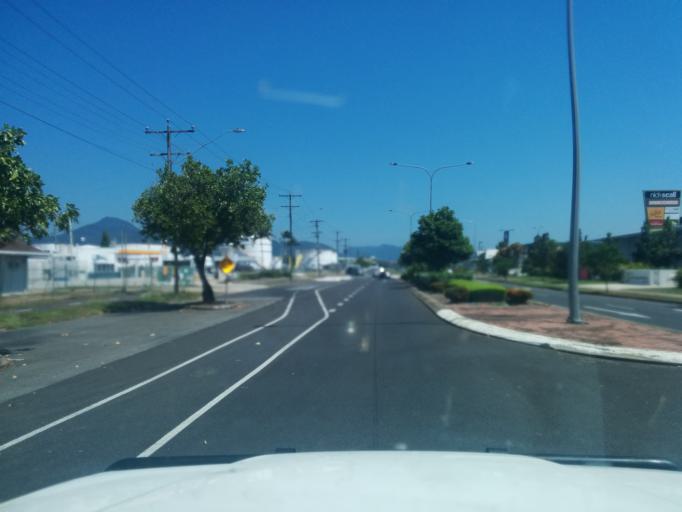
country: AU
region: Queensland
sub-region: Cairns
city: Cairns
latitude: -16.9316
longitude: 145.7729
